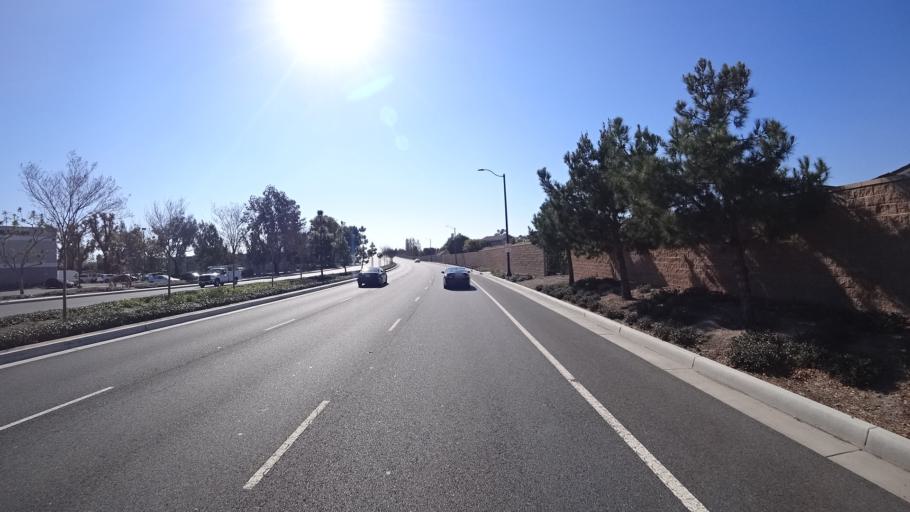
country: US
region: California
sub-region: Orange County
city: Tustin
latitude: 33.7180
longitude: -117.8106
